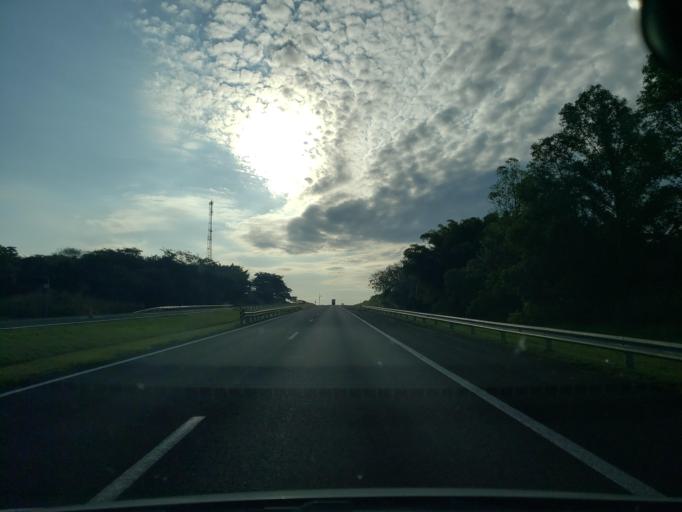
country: BR
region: Sao Paulo
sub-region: Valparaiso
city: Valparaiso
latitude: -21.1736
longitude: -50.9297
